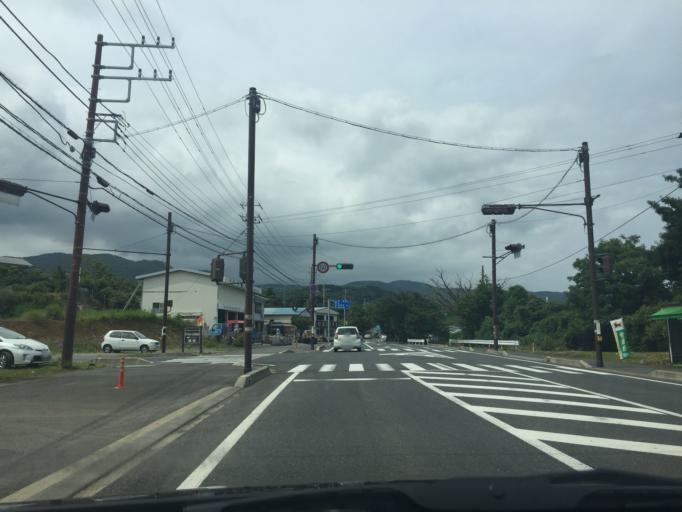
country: JP
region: Shizuoka
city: Shimoda
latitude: 34.7601
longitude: 139.0198
